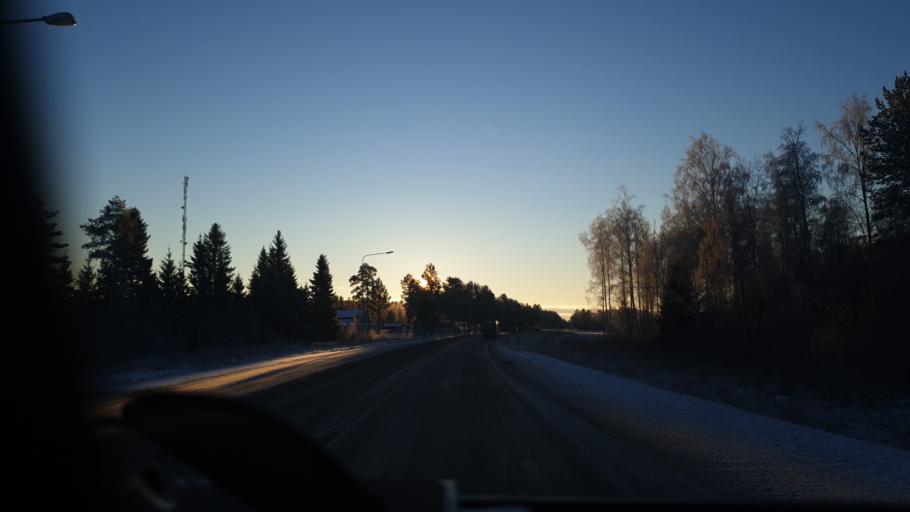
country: FI
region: Northern Ostrobothnia
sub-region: Ylivieska
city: Kalajoki
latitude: 64.2839
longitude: 23.9478
